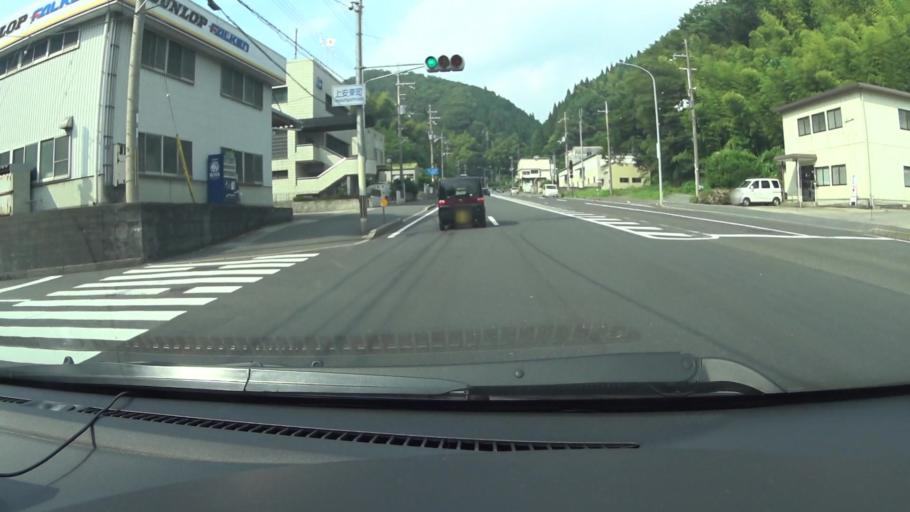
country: JP
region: Kyoto
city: Maizuru
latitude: 35.4572
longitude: 135.3511
